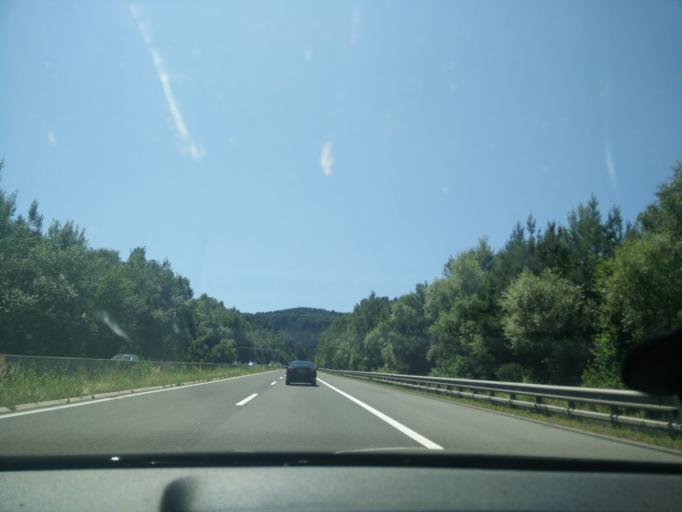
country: AT
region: Lower Austria
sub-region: Politischer Bezirk Neunkirchen
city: Edlitz
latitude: 47.5990
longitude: 16.1235
